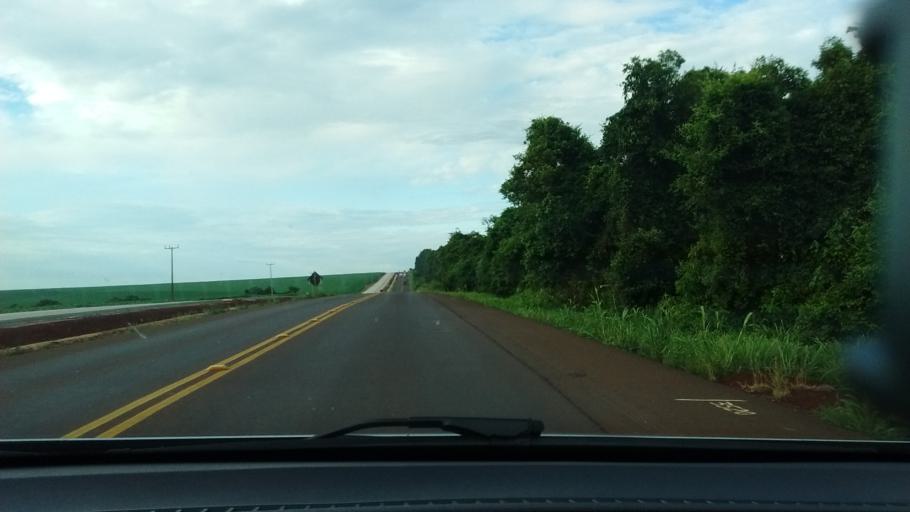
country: BR
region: Parana
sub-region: Cascavel
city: Cascavel
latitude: -25.0486
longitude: -53.5572
